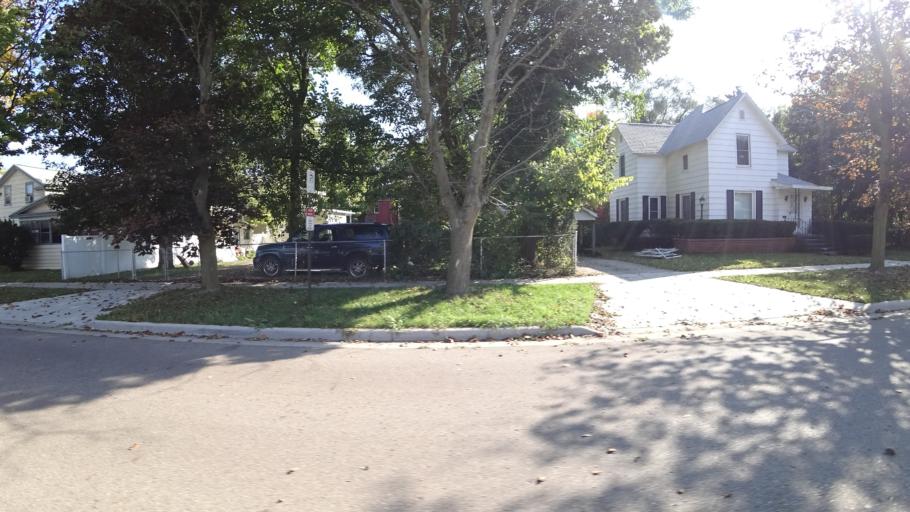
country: US
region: Michigan
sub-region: Saint Joseph County
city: Three Rivers
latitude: 41.9422
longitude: -85.6370
